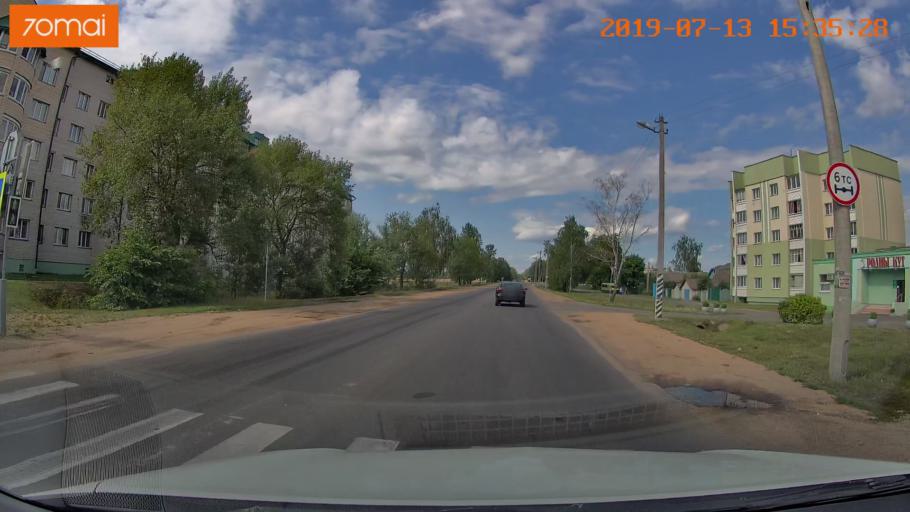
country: BY
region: Mogilev
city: Babruysk
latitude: 53.1235
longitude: 29.1665
